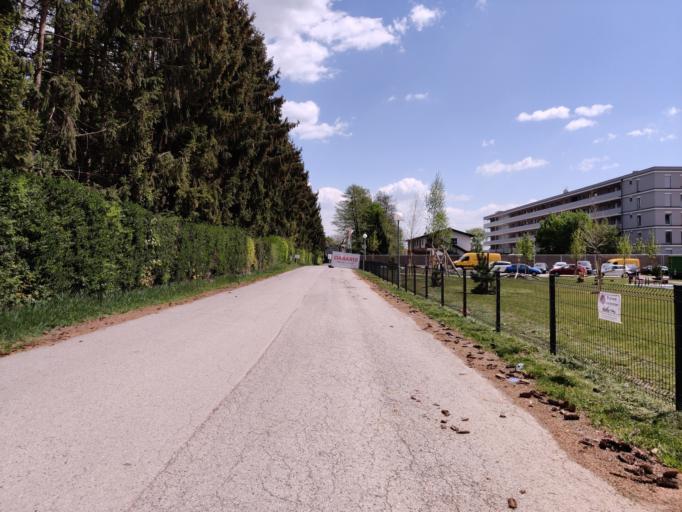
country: AT
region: Styria
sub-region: Graz Stadt
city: Wetzelsdorf
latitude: 47.0392
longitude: 15.3934
